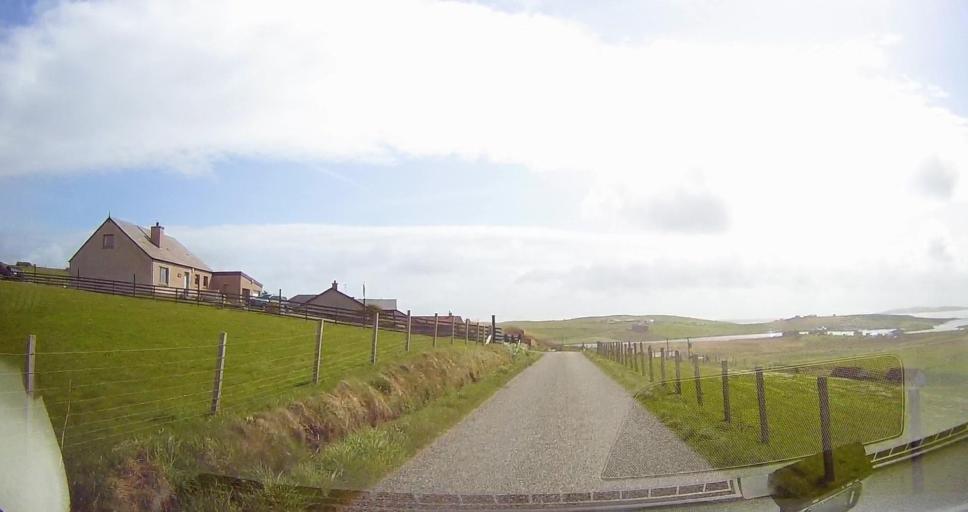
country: GB
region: Scotland
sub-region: Shetland Islands
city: Sandwick
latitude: 60.0496
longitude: -1.2200
